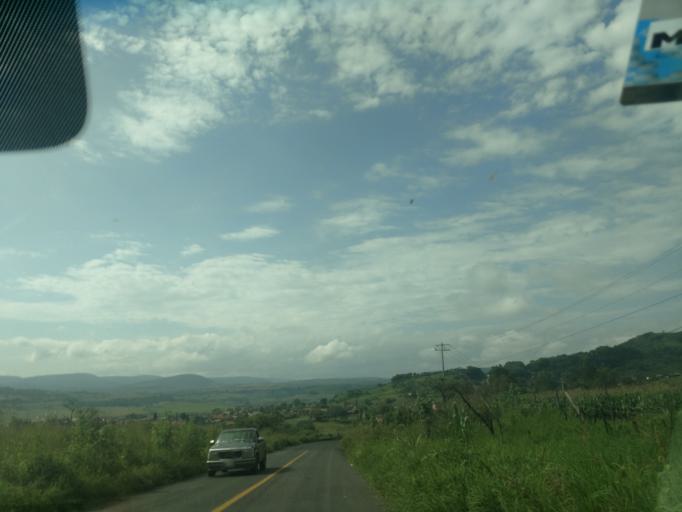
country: MX
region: Jalisco
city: El Salto
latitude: 20.4252
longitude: -104.4979
